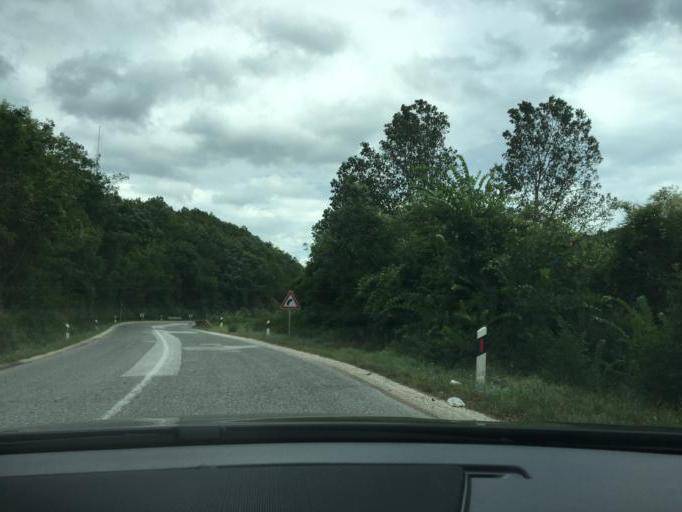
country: MK
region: Kriva Palanka
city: Kriva Palanka
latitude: 42.1895
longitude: 22.2930
